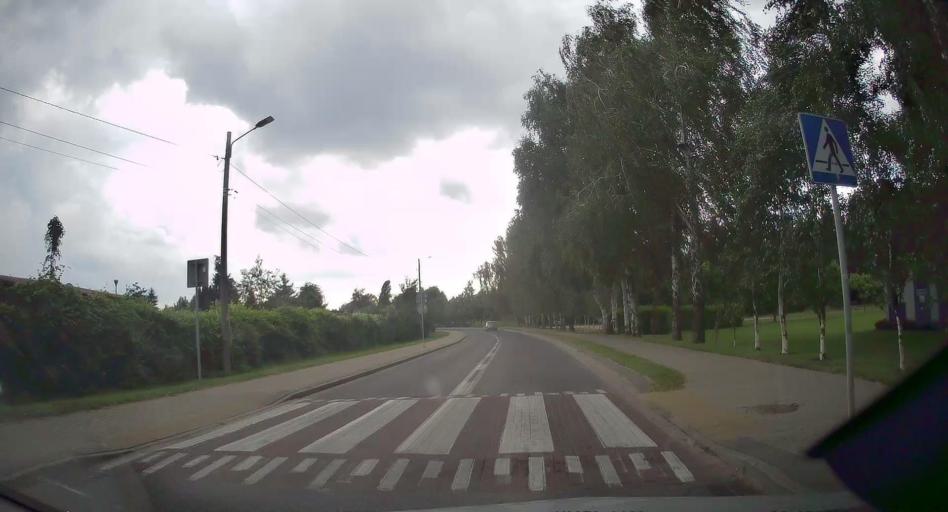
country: PL
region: Lodz Voivodeship
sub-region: Powiat rawski
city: Rawa Mazowiecka
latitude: 51.7533
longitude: 20.2329
